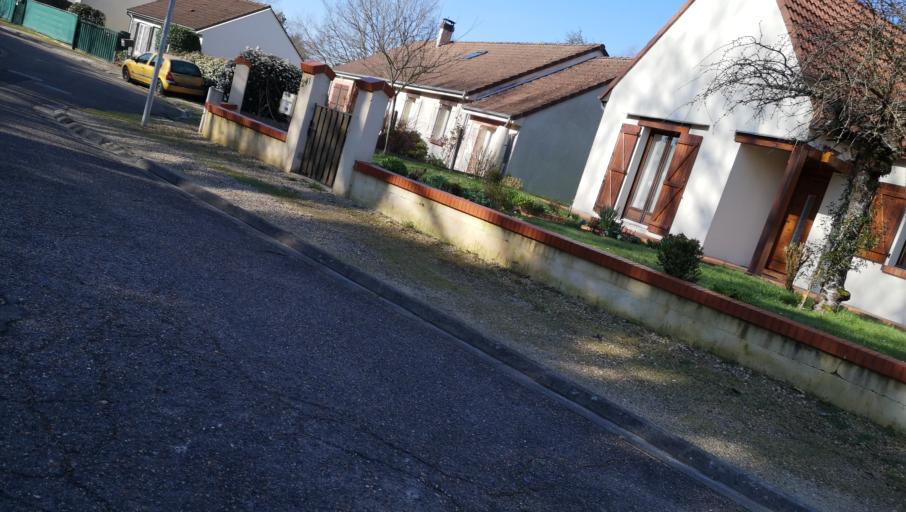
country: FR
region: Centre
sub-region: Departement du Loiret
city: Chanteau
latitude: 47.9663
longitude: 1.9694
